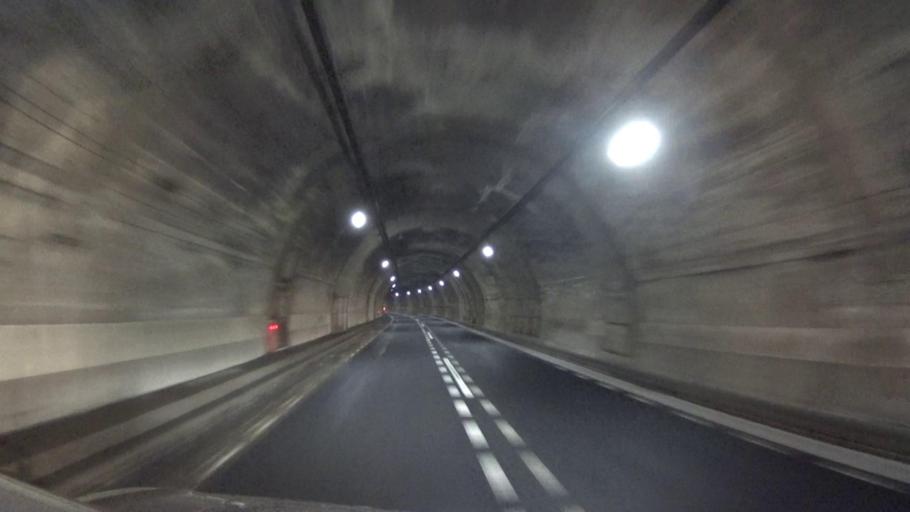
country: JP
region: Hokkaido
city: Otaru
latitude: 43.1640
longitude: 141.0959
